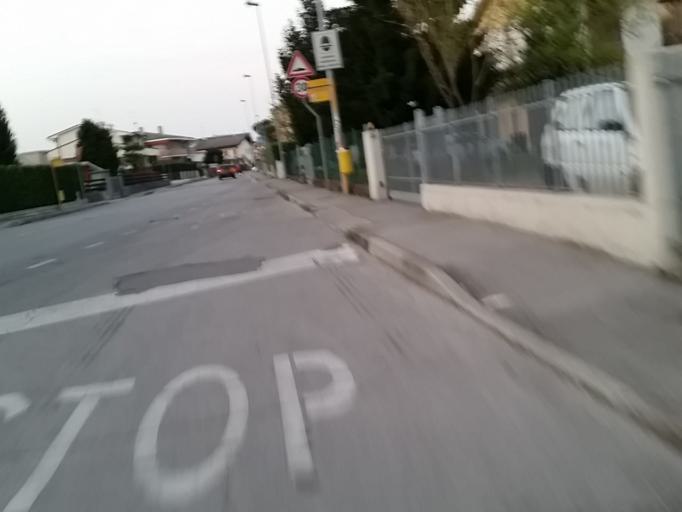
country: IT
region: Veneto
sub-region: Provincia di Padova
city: Mandriola-Sant'Agostino
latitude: 45.3705
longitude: 11.8569
